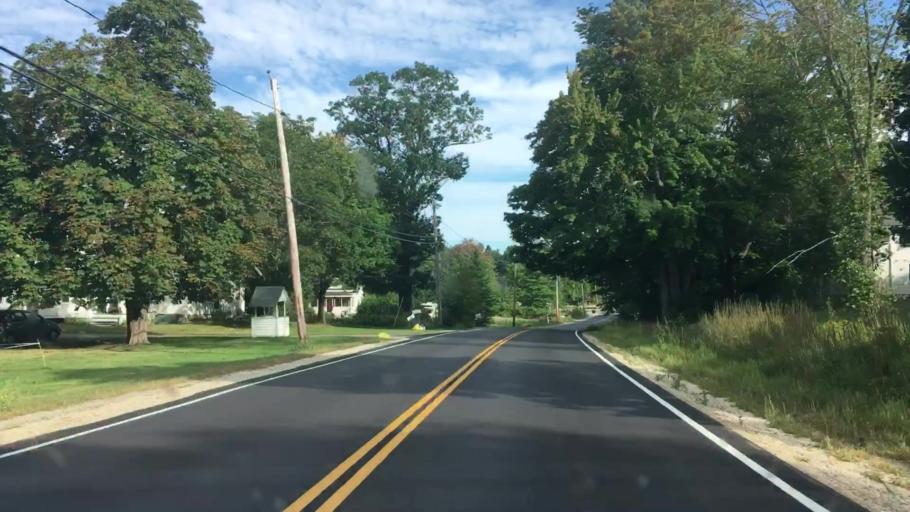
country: US
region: Maine
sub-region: Cumberland County
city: Cumberland Center
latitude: 43.7785
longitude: -70.3031
